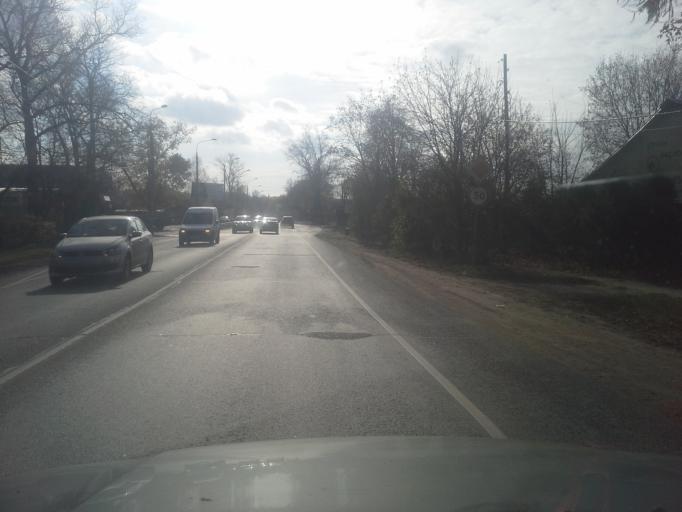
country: RU
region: Moskovskaya
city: Zvenigorod
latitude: 55.7227
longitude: 36.8634
